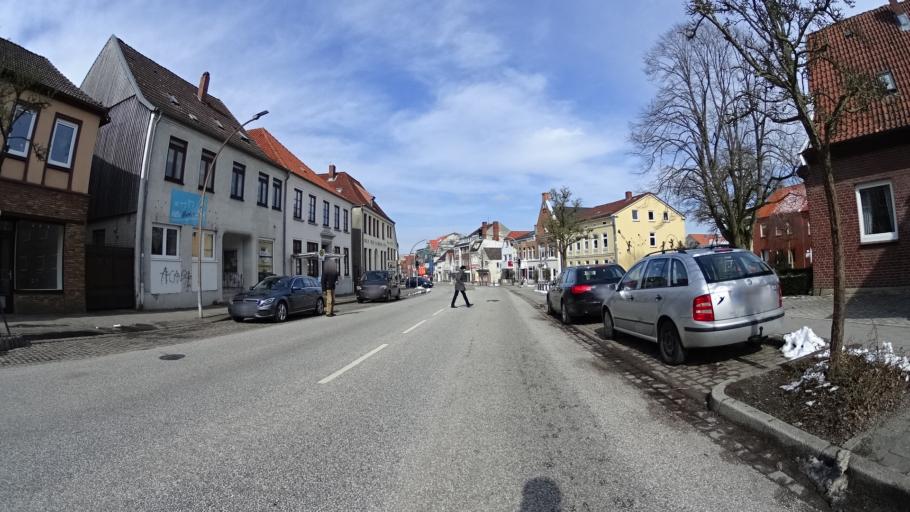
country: DE
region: Schleswig-Holstein
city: Preetz
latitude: 54.2322
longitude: 10.2811
